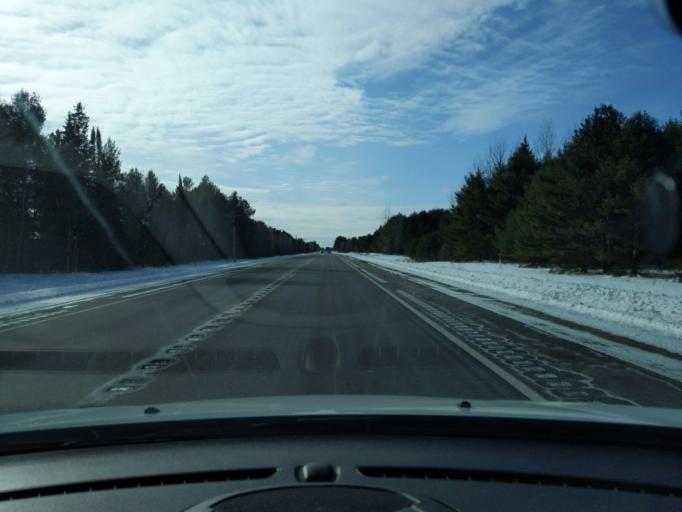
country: US
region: Wisconsin
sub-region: Sawyer County
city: Little Round Lake
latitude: 46.1072
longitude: -91.3755
